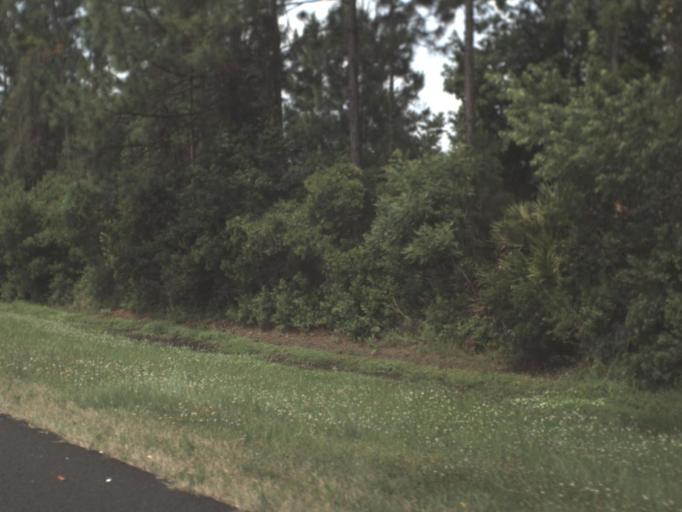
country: US
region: Florida
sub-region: Saint Johns County
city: Fruit Cove
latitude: 30.0842
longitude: -81.7067
